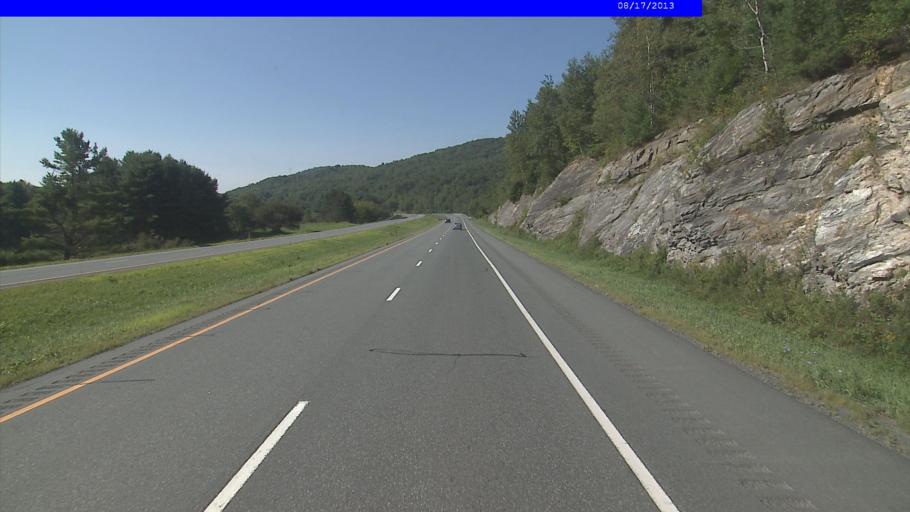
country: US
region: Vermont
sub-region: Windsor County
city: Windsor
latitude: 43.5032
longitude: -72.4090
